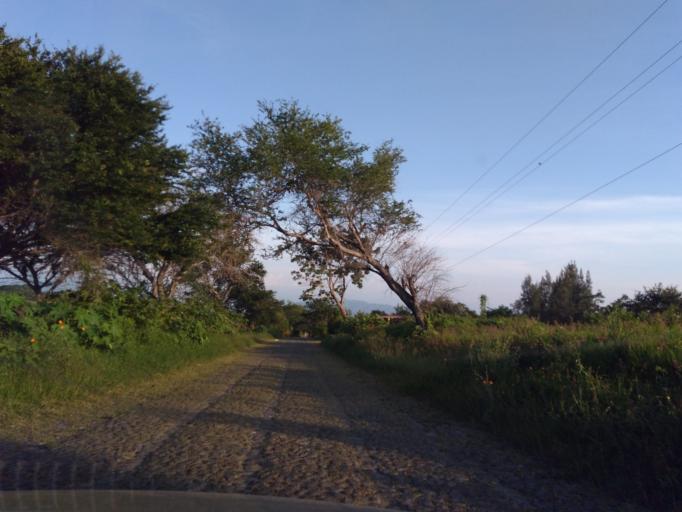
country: MX
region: Jalisco
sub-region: Tonila
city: San Marcos
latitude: 19.4521
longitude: -103.5140
